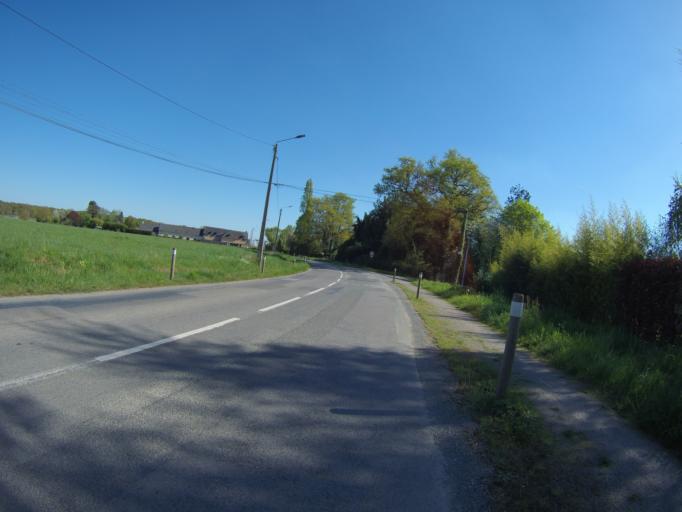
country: FR
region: Brittany
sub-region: Departement d'Ille-et-Vilaine
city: Chantepie
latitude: 48.0681
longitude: -1.6262
